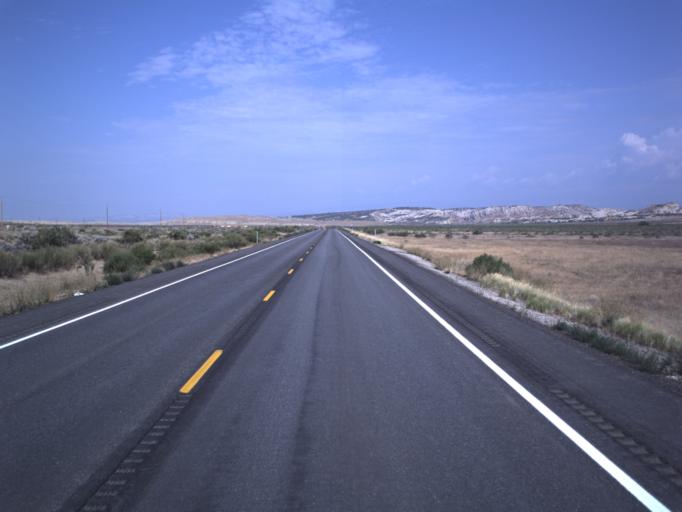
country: US
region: Utah
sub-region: Uintah County
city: Naples
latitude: 40.3031
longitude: -109.2014
